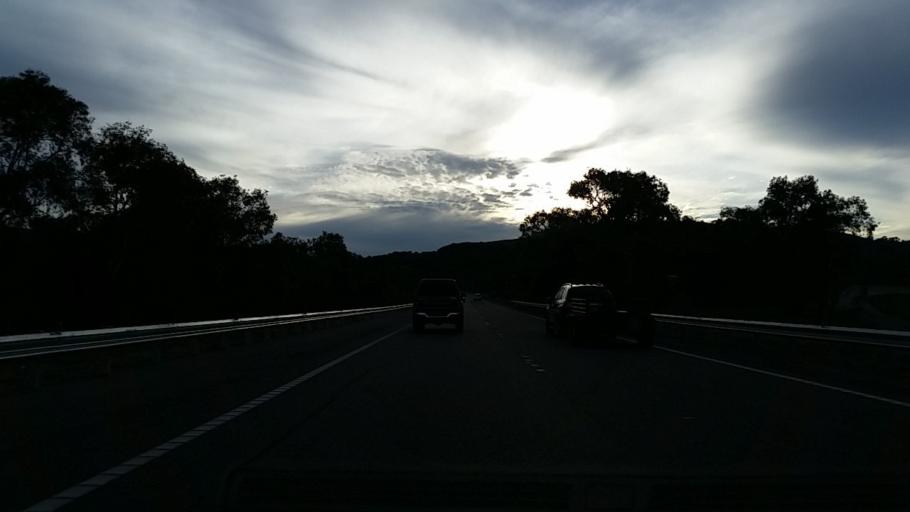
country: AU
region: South Australia
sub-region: Mount Barker
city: Callington
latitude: -35.1143
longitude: 138.9901
